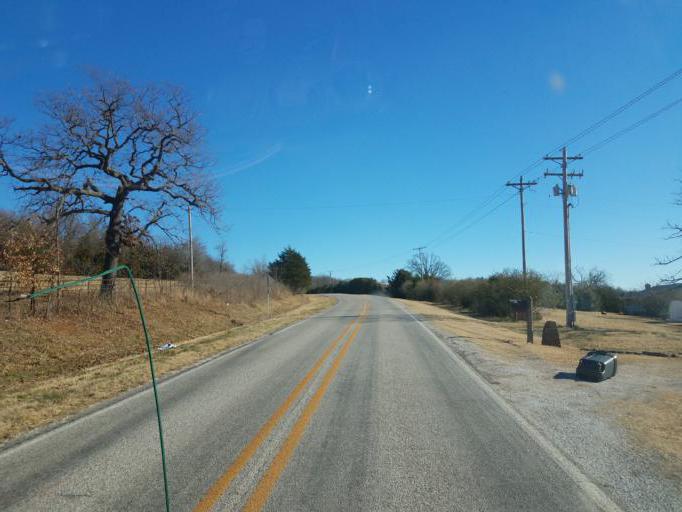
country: US
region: Arkansas
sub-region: Washington County
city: Elkins
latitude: 36.0254
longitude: -93.9926
